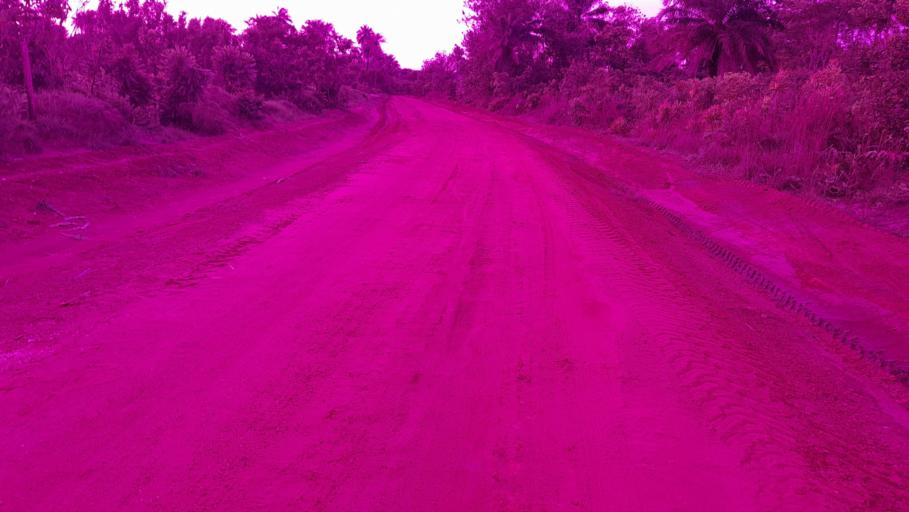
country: GN
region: Boke
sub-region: Boffa
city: Boffa
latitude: 10.0702
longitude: -13.8675
